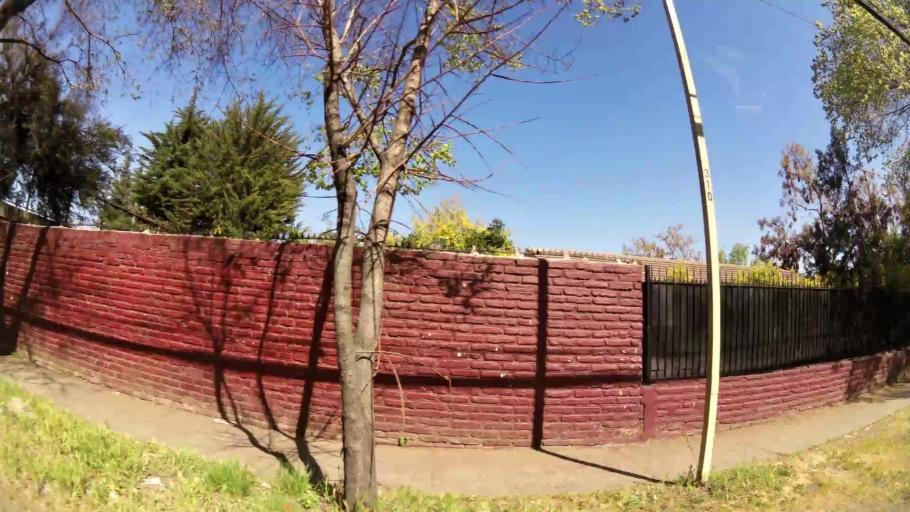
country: CL
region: Santiago Metropolitan
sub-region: Provincia de Santiago
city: Villa Presidente Frei, Nunoa, Santiago, Chile
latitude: -33.4098
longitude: -70.5364
